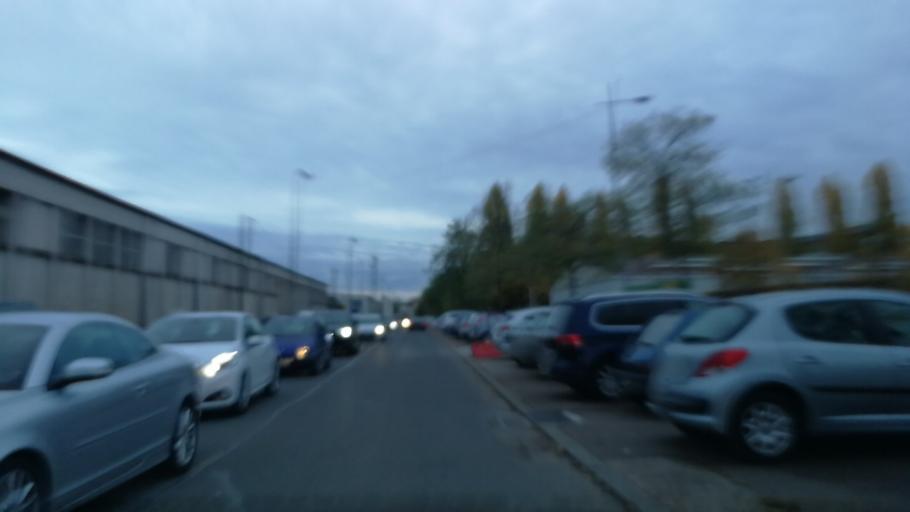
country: FR
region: Bourgogne
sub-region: Departement de la Cote-d'Or
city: Saint-Apollinaire
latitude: 47.3340
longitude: 5.0573
